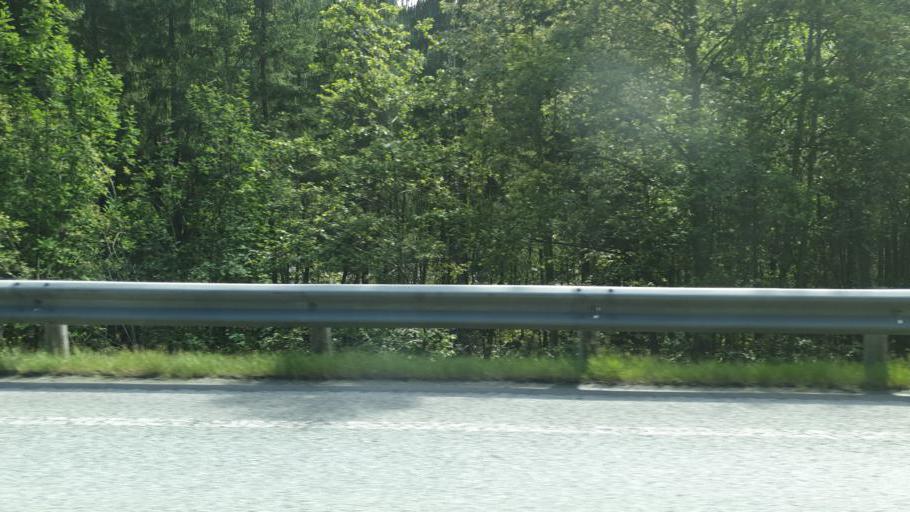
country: NO
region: Sor-Trondelag
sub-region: Midtre Gauldal
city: Storen
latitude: 63.0227
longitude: 10.2499
